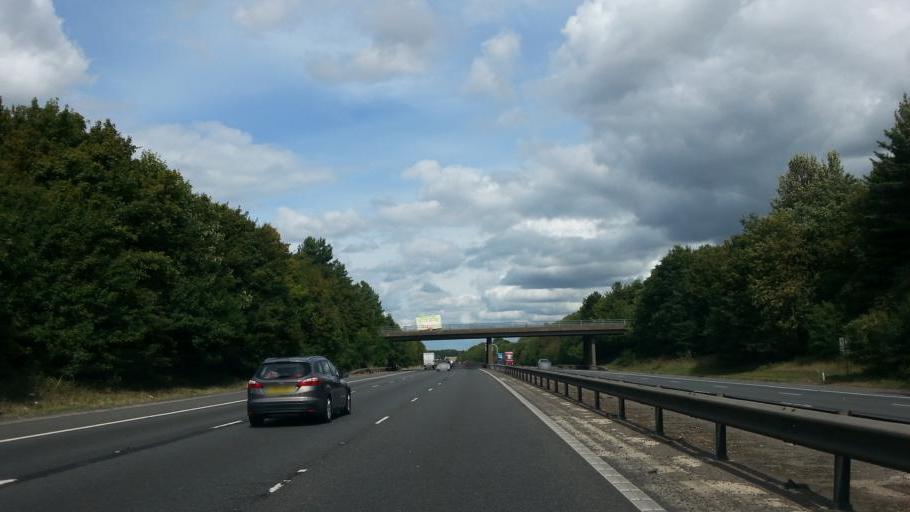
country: GB
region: England
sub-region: Hertfordshire
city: Sawbridgeworth
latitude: 51.7815
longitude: 0.1673
